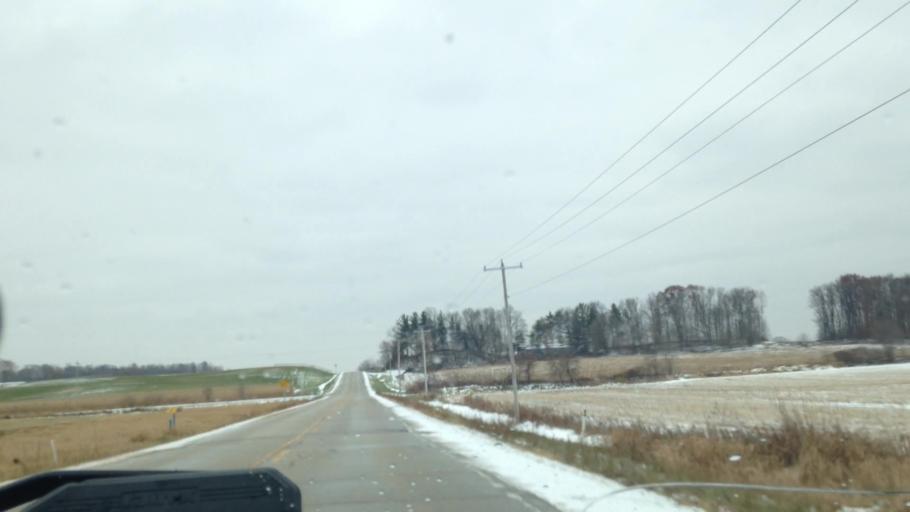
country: US
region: Wisconsin
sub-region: Dodge County
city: Mayville
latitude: 43.4555
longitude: -88.4999
